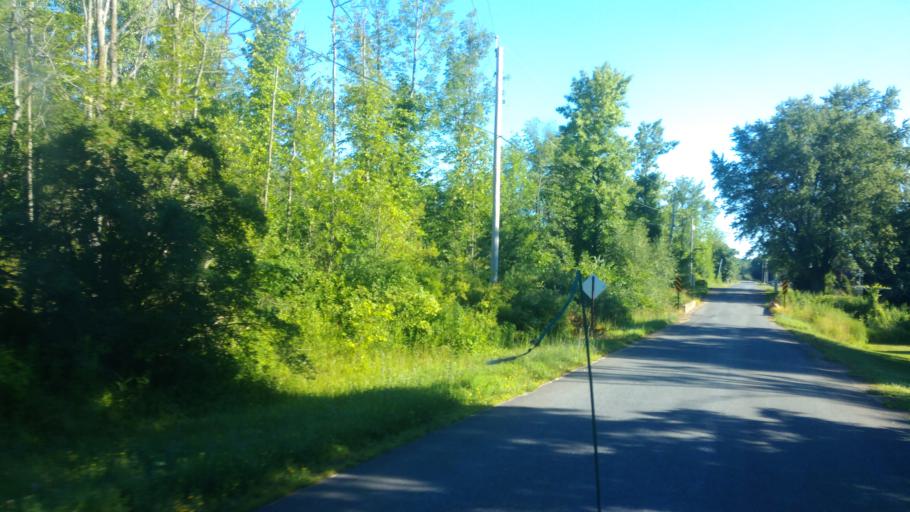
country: US
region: New York
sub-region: Wayne County
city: Sodus
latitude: 43.1952
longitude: -77.0956
